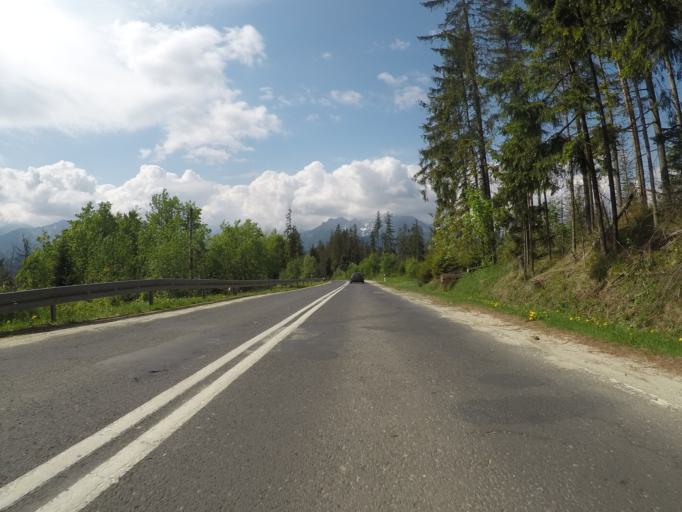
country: PL
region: Lesser Poland Voivodeship
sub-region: Powiat tatrzanski
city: Bukowina Tatrzanska
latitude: 49.2977
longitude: 20.1158
